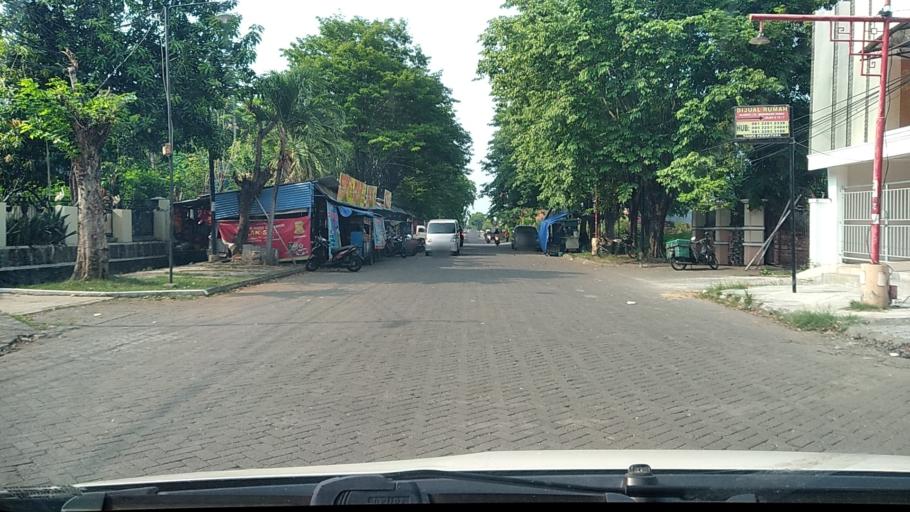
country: ID
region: Central Java
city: Semarang
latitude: -6.9685
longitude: 110.3964
